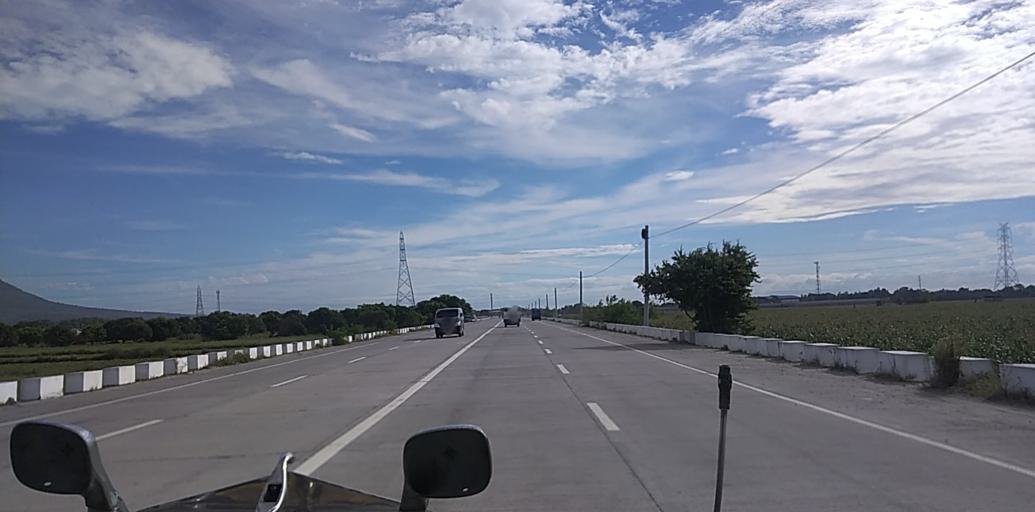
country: PH
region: Central Luzon
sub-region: Province of Pampanga
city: Anao
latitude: 15.1350
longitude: 120.6862
